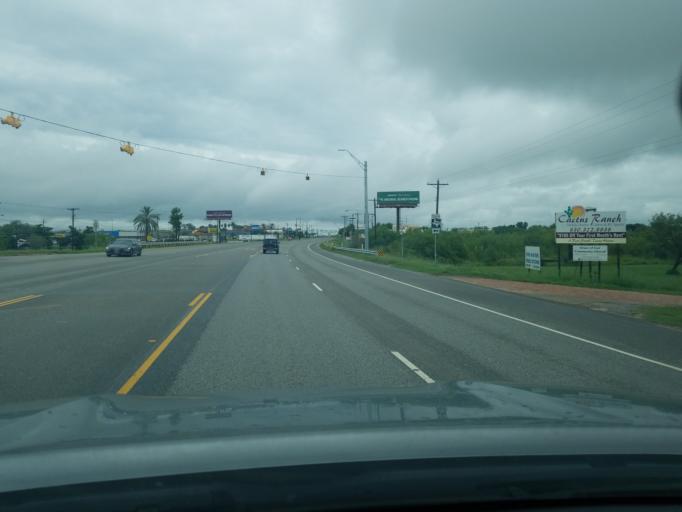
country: US
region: Texas
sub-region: Dimmit County
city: Carrizo Springs
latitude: 28.5393
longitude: -99.8494
